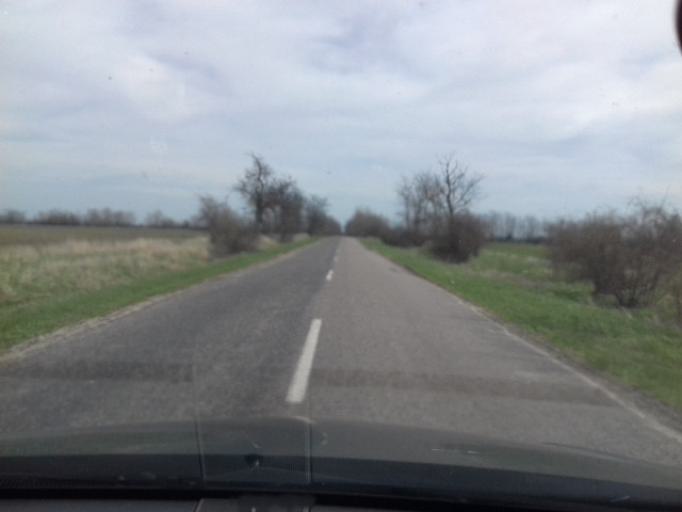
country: HU
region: Jasz-Nagykun-Szolnok
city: Cserkeszolo
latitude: 46.9004
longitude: 20.1758
